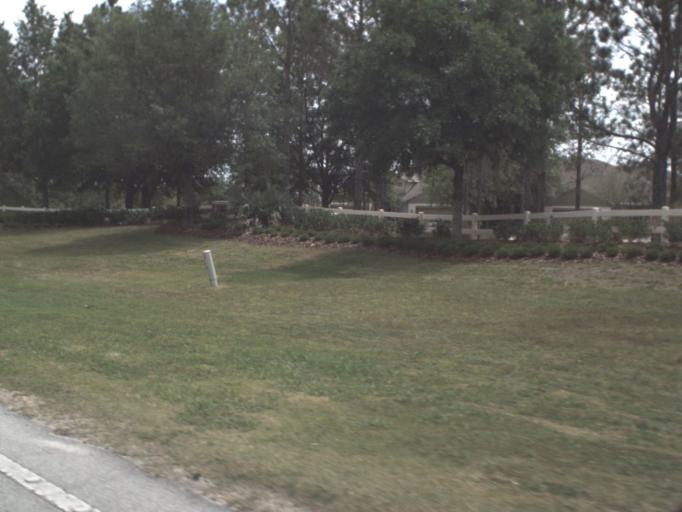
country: US
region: Florida
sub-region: Lake County
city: Mount Plymouth
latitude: 28.8513
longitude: -81.5592
